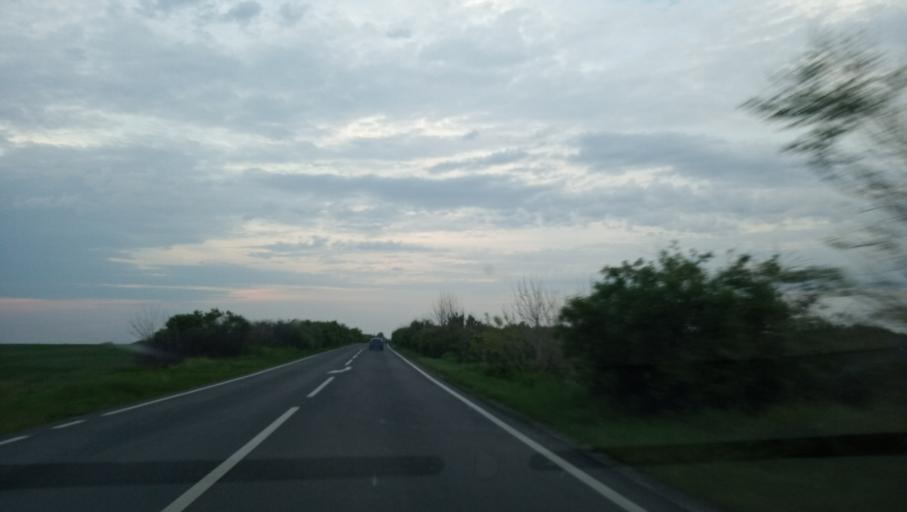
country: RO
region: Timis
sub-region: Comuna Voiteg
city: Voiteg
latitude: 45.4963
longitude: 21.2363
